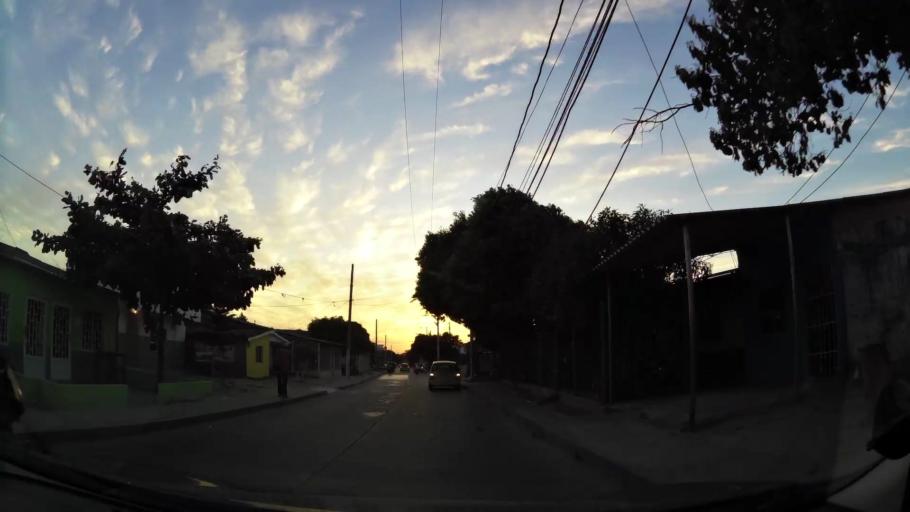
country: CO
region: Atlantico
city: Barranquilla
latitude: 10.9593
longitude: -74.8209
